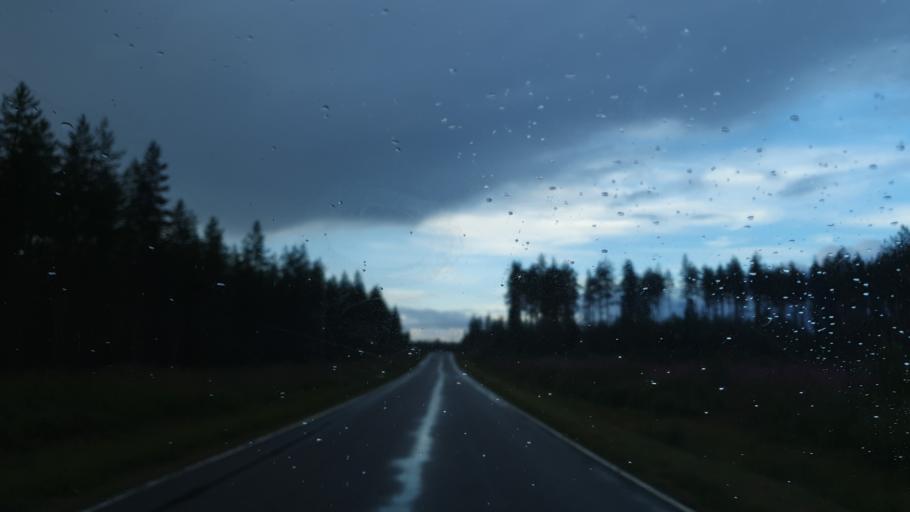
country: FI
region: North Karelia
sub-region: Pielisen Karjala
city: Lieksa
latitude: 63.6579
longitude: 29.8641
